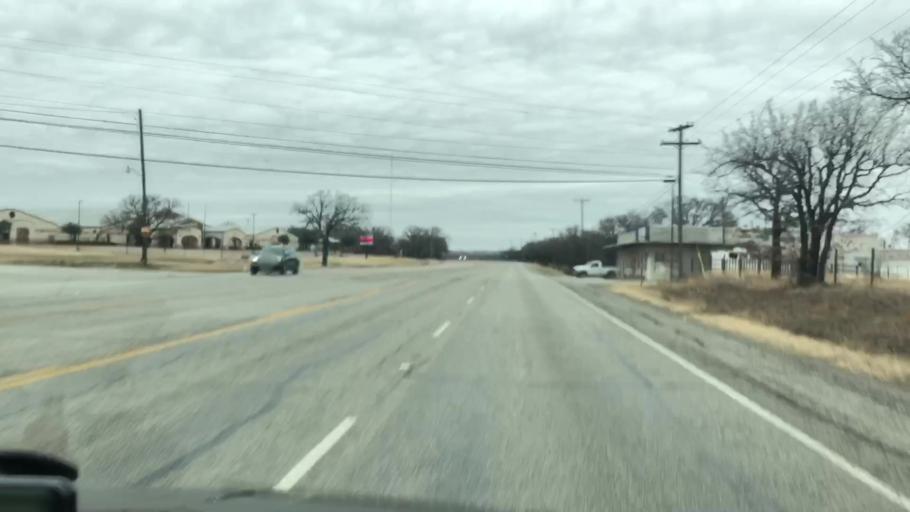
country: US
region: Texas
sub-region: Jack County
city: Jacksboro
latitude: 33.2277
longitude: -98.1741
